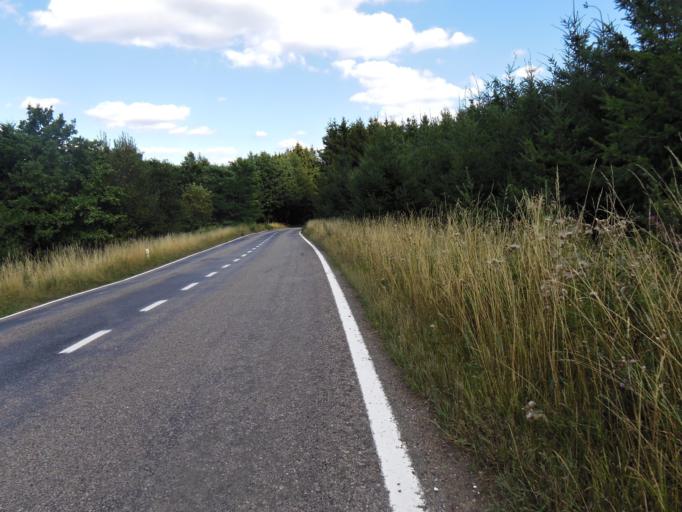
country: BE
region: Wallonia
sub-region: Province de Namur
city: Bievre
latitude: 49.8849
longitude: 4.9957
